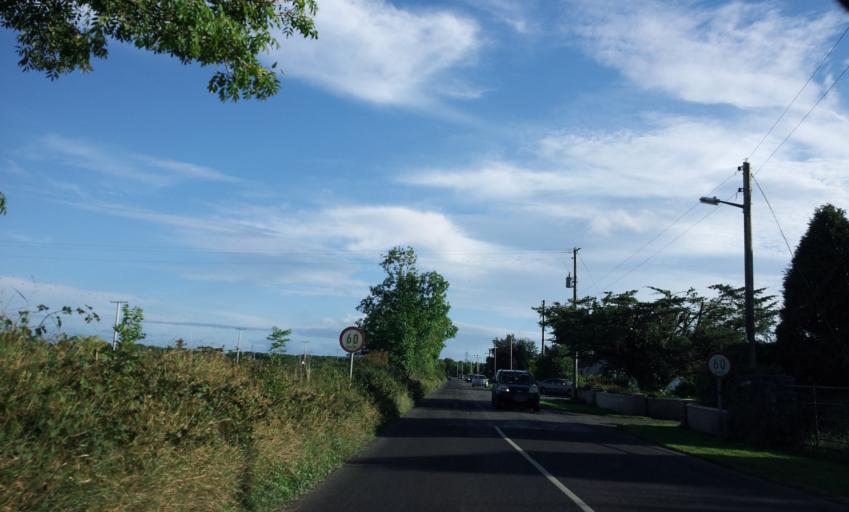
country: IE
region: Munster
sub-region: An Clar
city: Ennis
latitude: 52.9415
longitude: -9.0618
